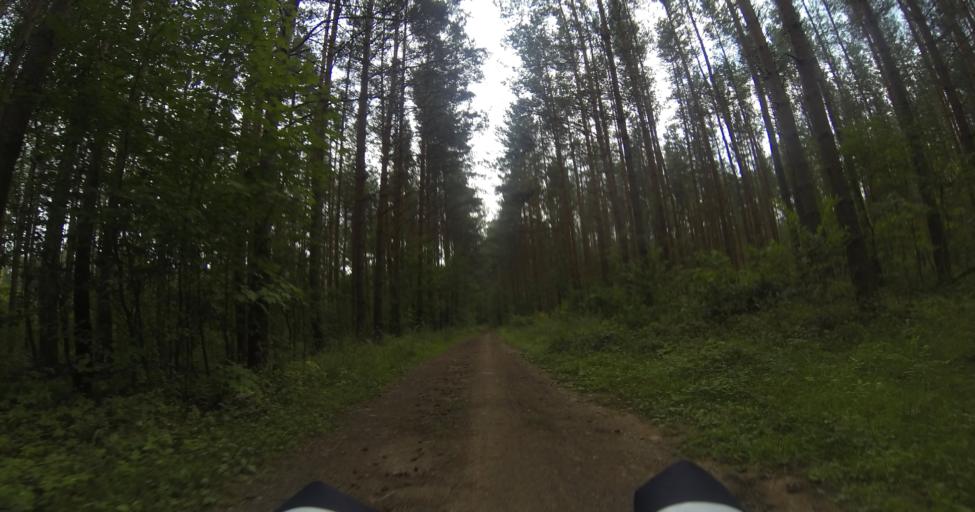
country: DE
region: Saxony
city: Weinbohla
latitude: 51.1745
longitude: 13.6092
